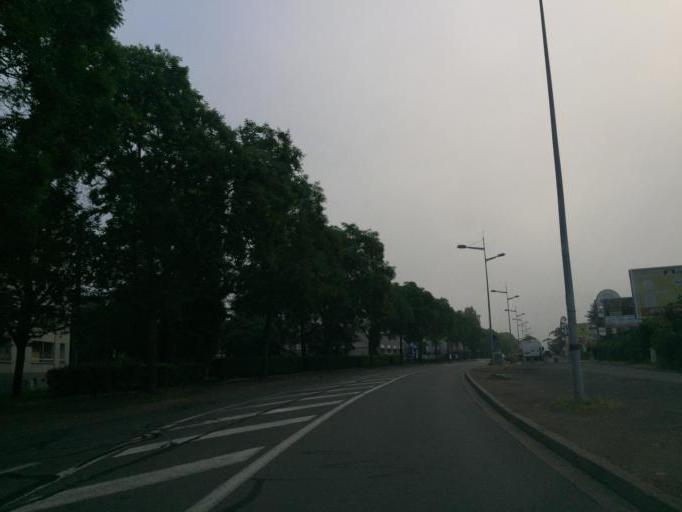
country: FR
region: Rhone-Alpes
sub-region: Departement de l'Ain
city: Jassans-Riottier
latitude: 45.9802
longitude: 4.7397
